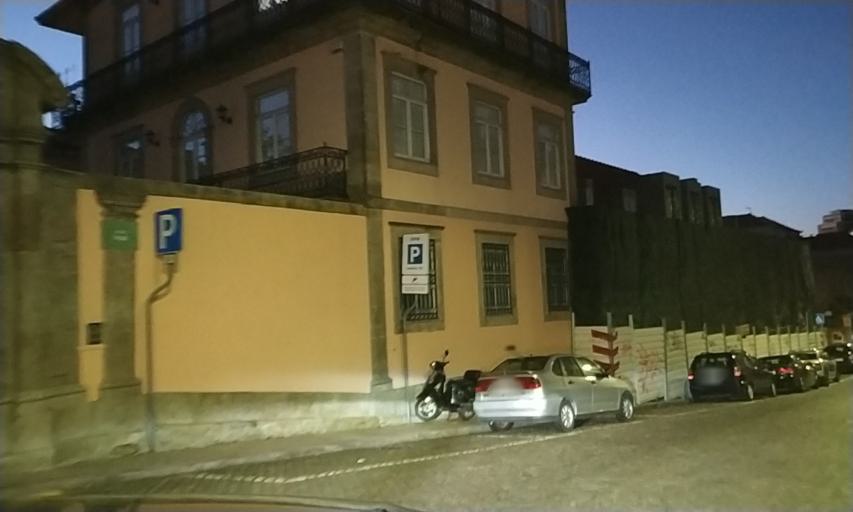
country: PT
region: Porto
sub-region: Porto
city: Porto
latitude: 41.1489
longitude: -8.6268
